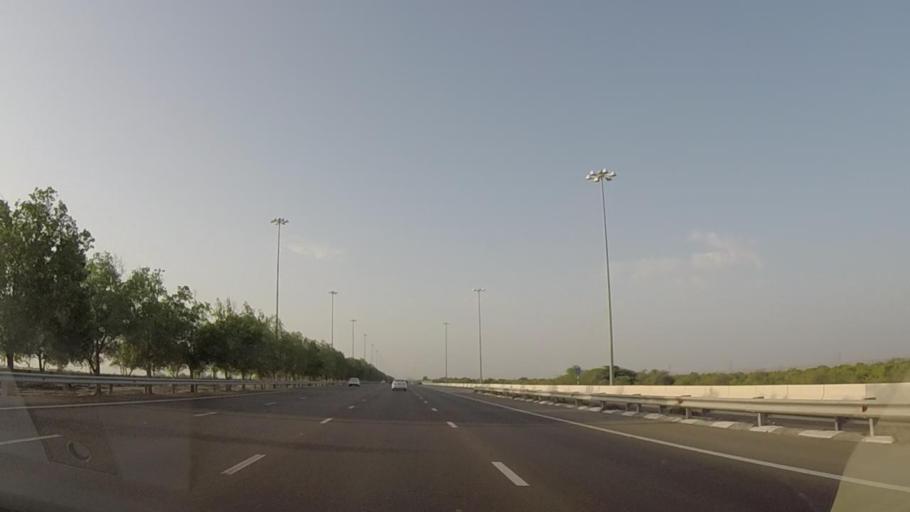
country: AE
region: Dubai
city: Dubai
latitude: 24.7955
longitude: 54.8615
